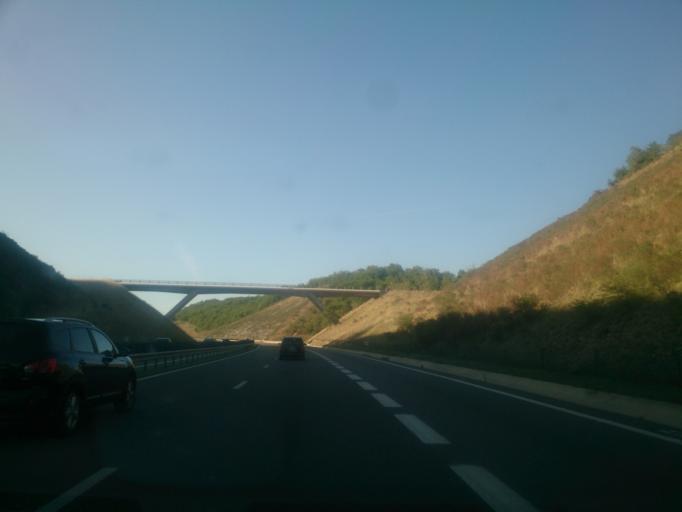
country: FR
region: Midi-Pyrenees
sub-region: Departement du Lot
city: Cahors
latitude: 44.4756
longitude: 1.5053
